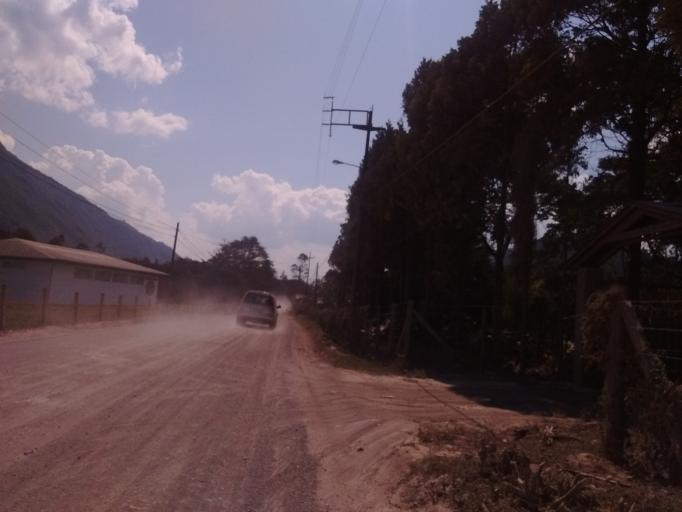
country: PE
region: Pasco
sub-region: Provincia de Oxapampa
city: Oxapampa
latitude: -10.5677
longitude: -75.4082
